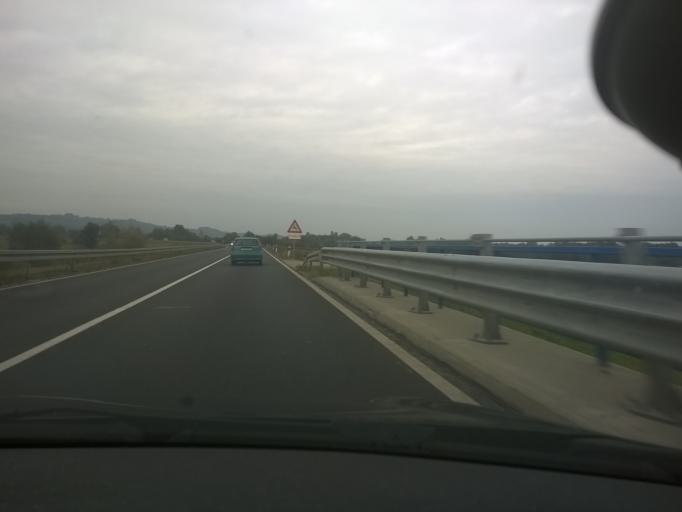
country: HR
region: Zagrebacka
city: Pojatno
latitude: 45.8915
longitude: 15.8217
